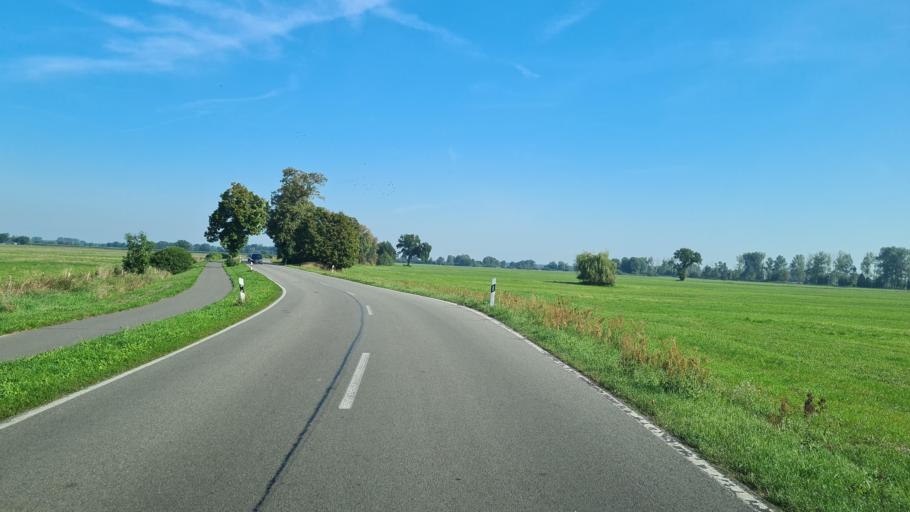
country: DE
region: Brandenburg
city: Friesack
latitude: 52.7458
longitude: 12.5816
